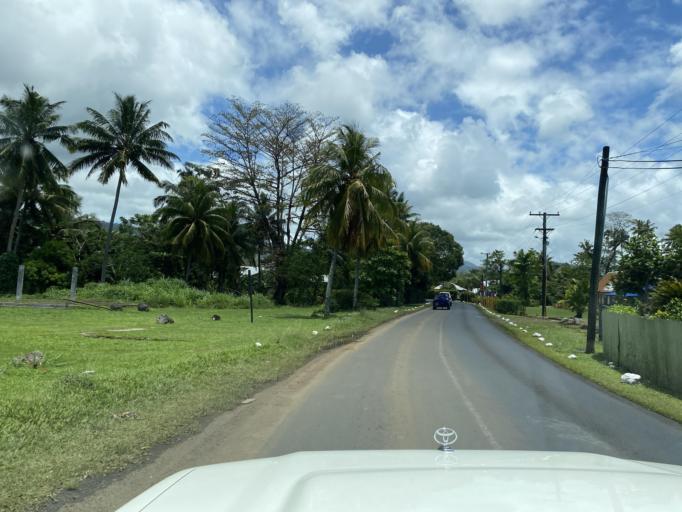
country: WS
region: Tuamasaga
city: Apia
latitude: -13.8499
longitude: -171.7793
